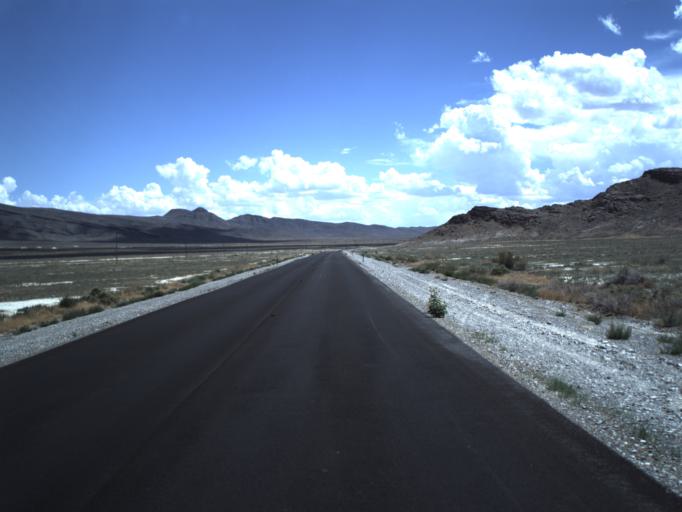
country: US
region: Utah
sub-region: Beaver County
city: Milford
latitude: 39.0674
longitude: -113.4536
